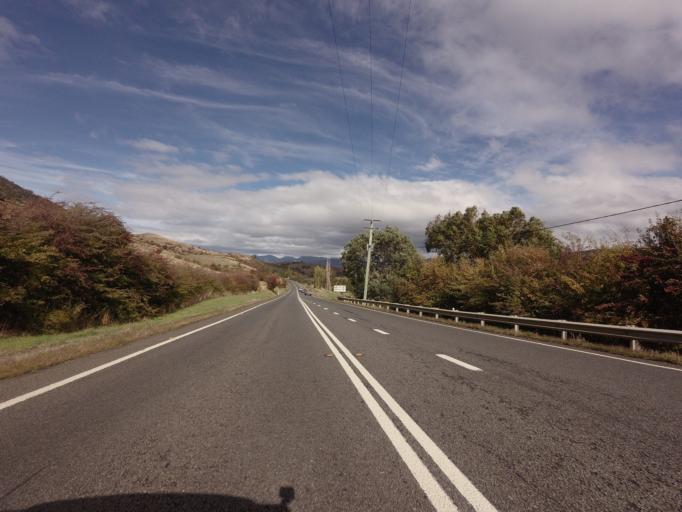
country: AU
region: Tasmania
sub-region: Derwent Valley
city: New Norfolk
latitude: -42.7219
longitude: 146.9495
